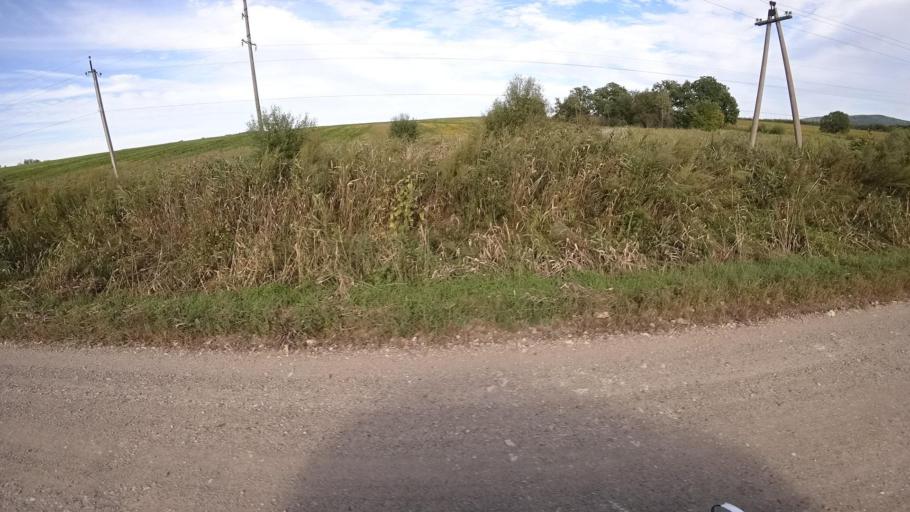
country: RU
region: Primorskiy
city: Dostoyevka
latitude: 44.3104
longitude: 133.4640
